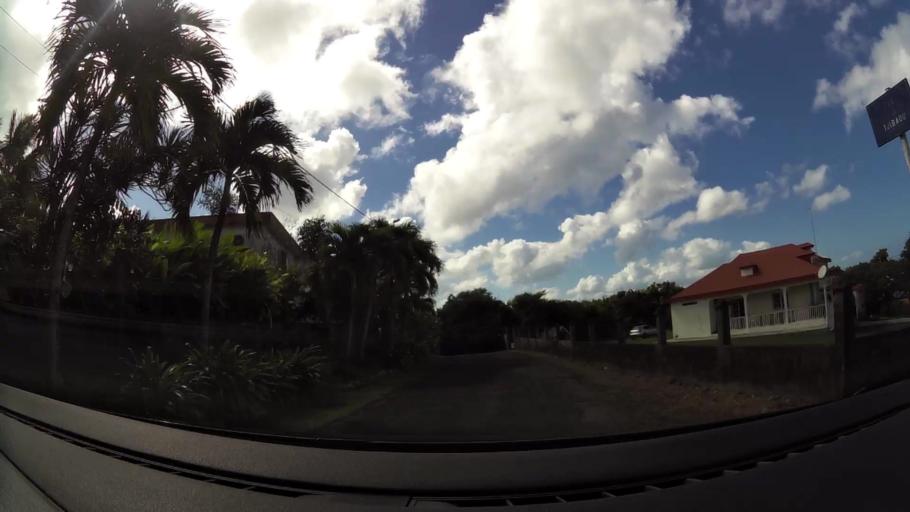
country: GP
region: Guadeloupe
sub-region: Guadeloupe
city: Port-Louis
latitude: 16.4219
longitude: -61.5260
